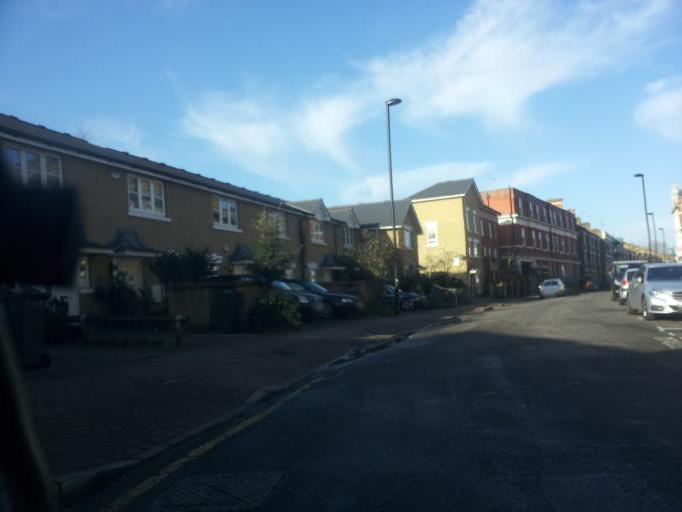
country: GB
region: England
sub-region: Greater London
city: Kennington
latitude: 51.4934
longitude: -0.1047
